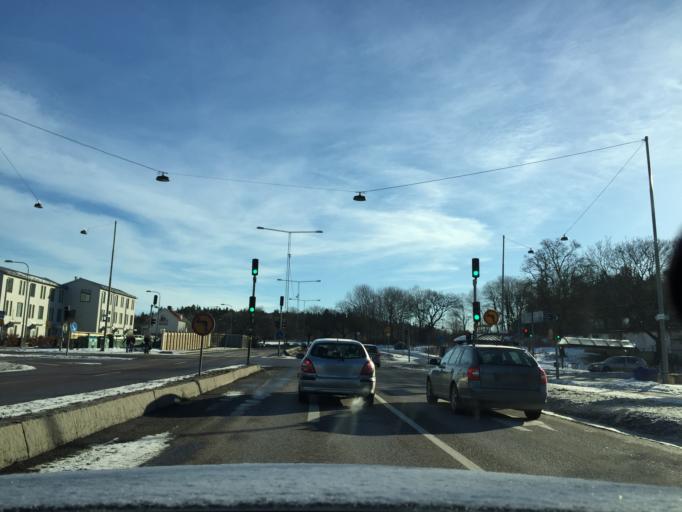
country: SE
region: Stockholm
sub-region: Stockholms Kommun
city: Bromma
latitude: 59.3427
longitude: 17.9062
